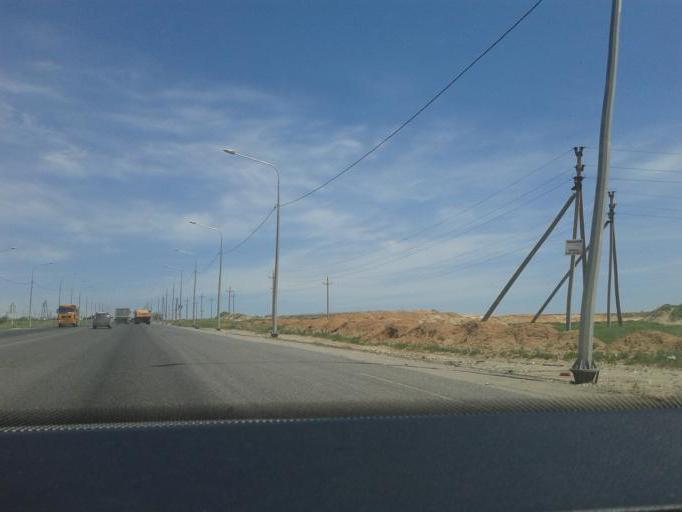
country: RU
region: Volgograd
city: Vodstroy
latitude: 48.8078
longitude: 44.5233
